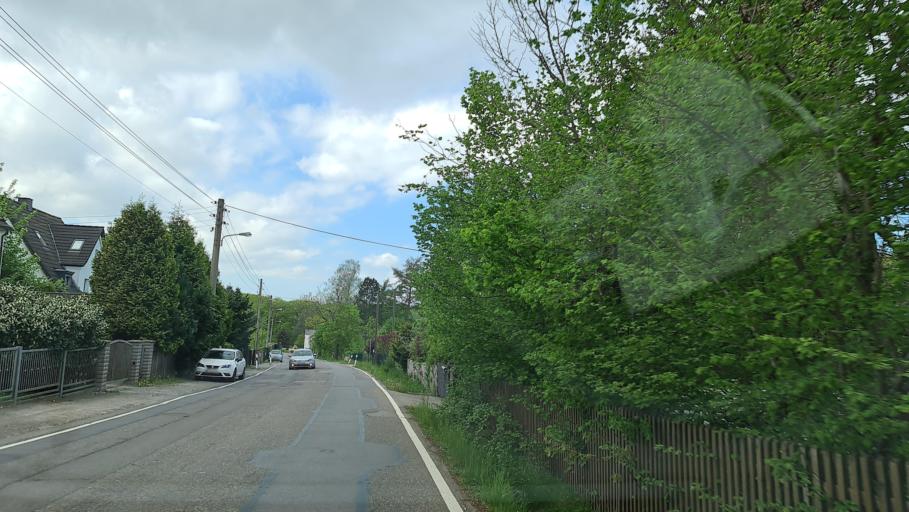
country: DE
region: Saxony
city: Hilbersdorf
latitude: 50.8330
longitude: 12.9878
